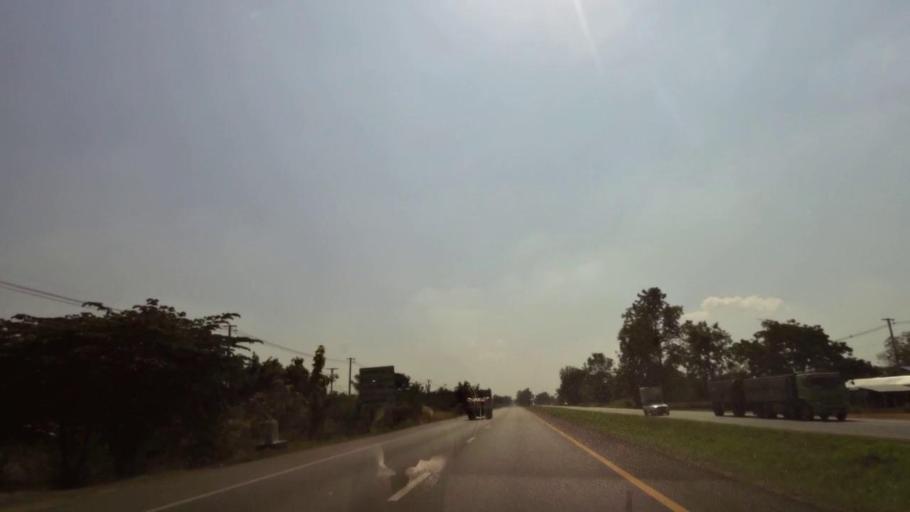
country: TH
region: Phichit
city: Bueng Na Rang
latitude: 16.2617
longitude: 100.1261
